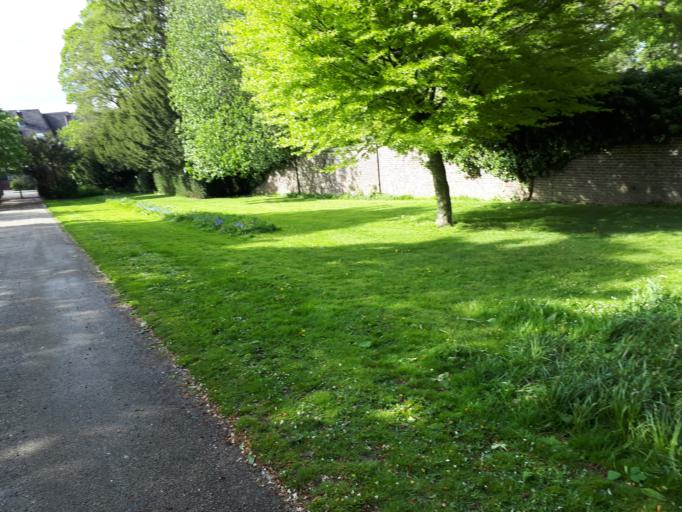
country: NL
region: Limburg
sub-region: Gemeente Vaals
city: Vaals
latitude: 50.7720
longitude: 6.0119
